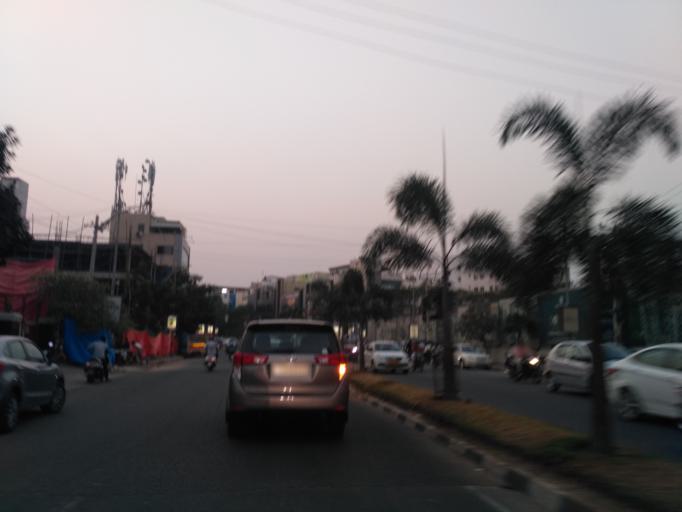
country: IN
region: Telangana
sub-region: Rangareddi
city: Kukatpalli
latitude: 17.4407
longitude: 78.3978
